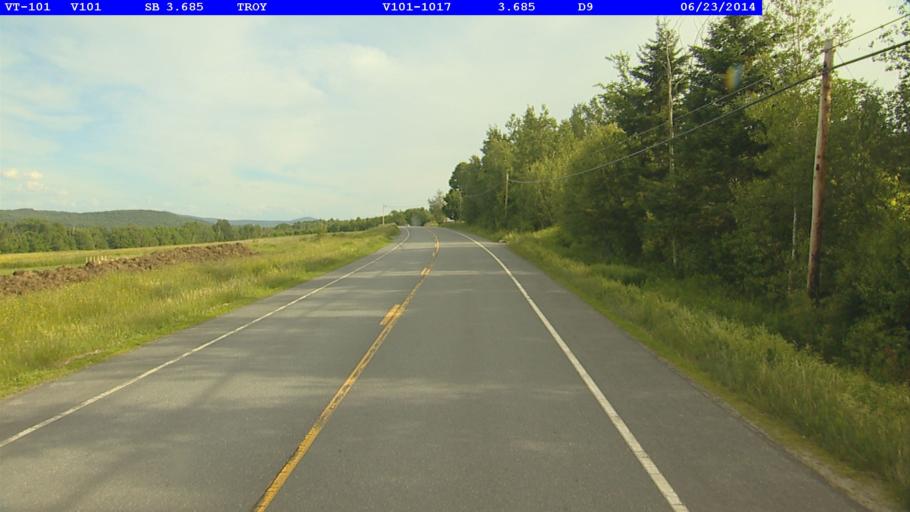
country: US
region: Vermont
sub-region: Orleans County
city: Newport
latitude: 44.9555
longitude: -72.4124
